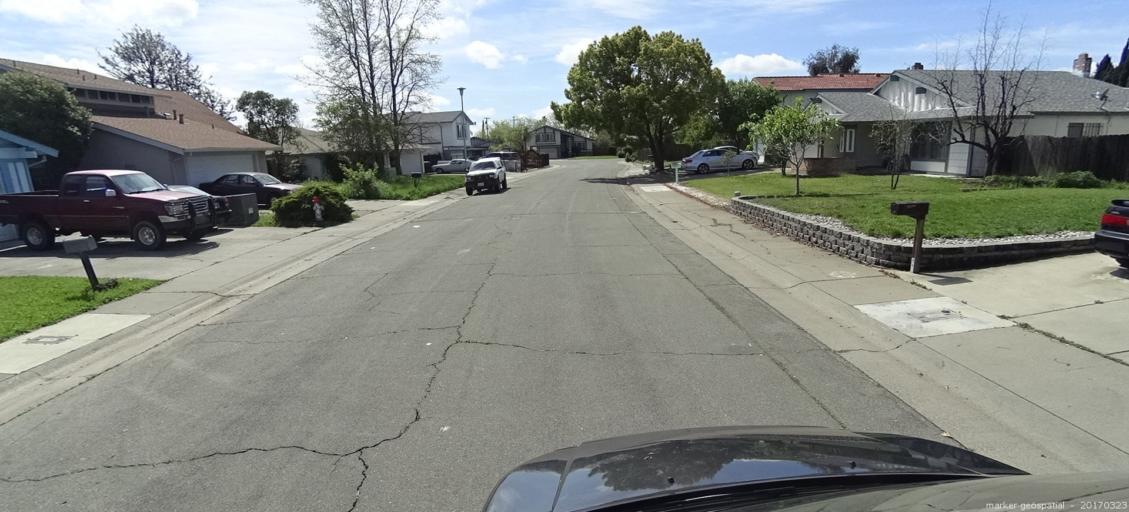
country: US
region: California
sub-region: Sacramento County
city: Florin
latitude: 38.5056
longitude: -121.4238
